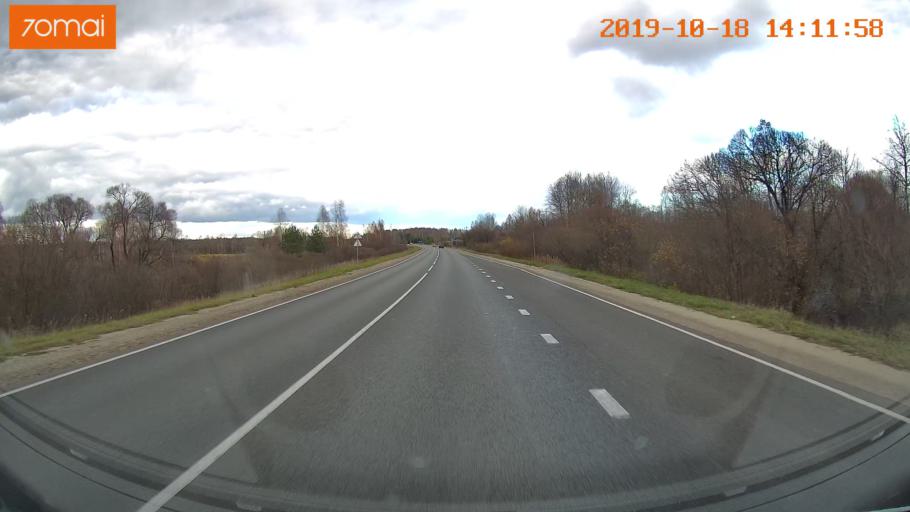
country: RU
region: Rjazan
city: Spas-Klepiki
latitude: 55.1410
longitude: 40.2390
